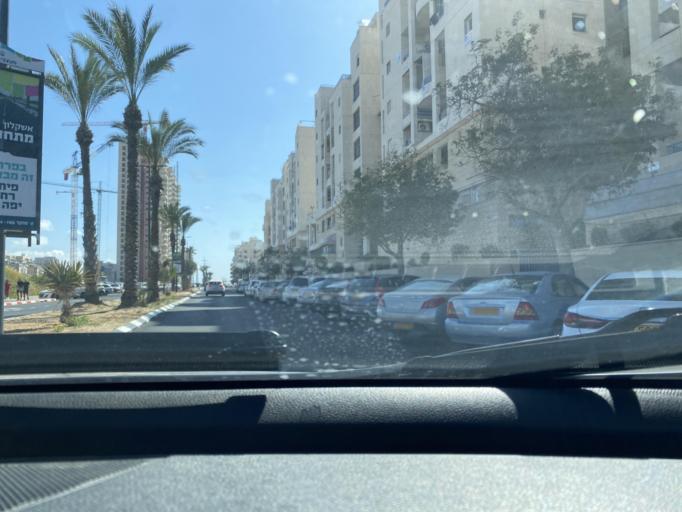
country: IL
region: Southern District
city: Ashqelon
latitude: 31.6825
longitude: 34.5598
